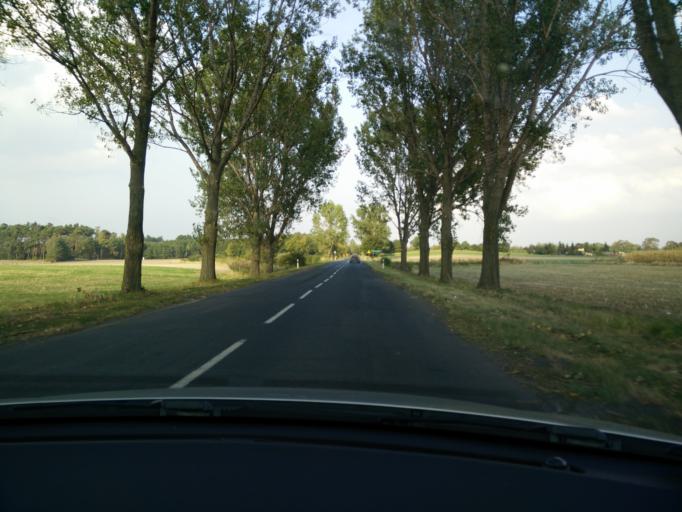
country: PL
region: Greater Poland Voivodeship
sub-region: Powiat wrzesinski
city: Miloslaw
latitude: 52.2758
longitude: 17.4704
